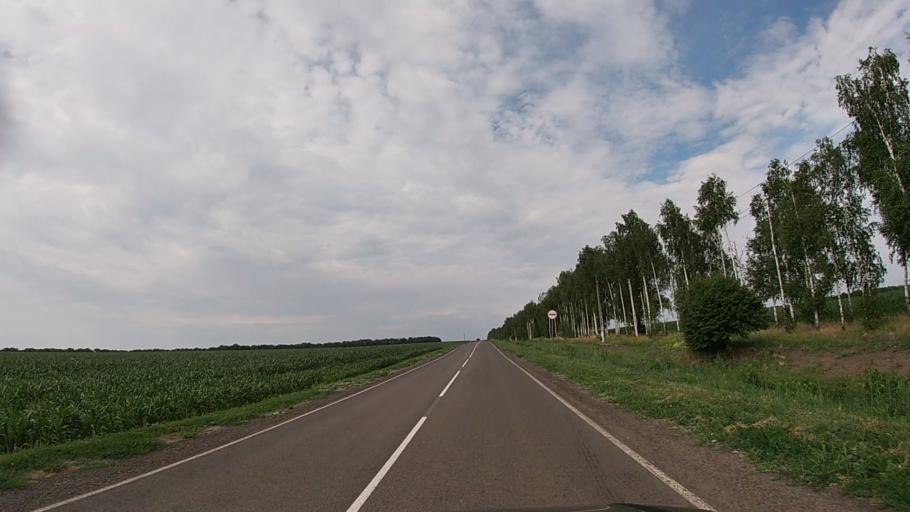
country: RU
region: Belgorod
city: Krasnaya Yaruga
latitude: 50.8246
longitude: 35.4661
